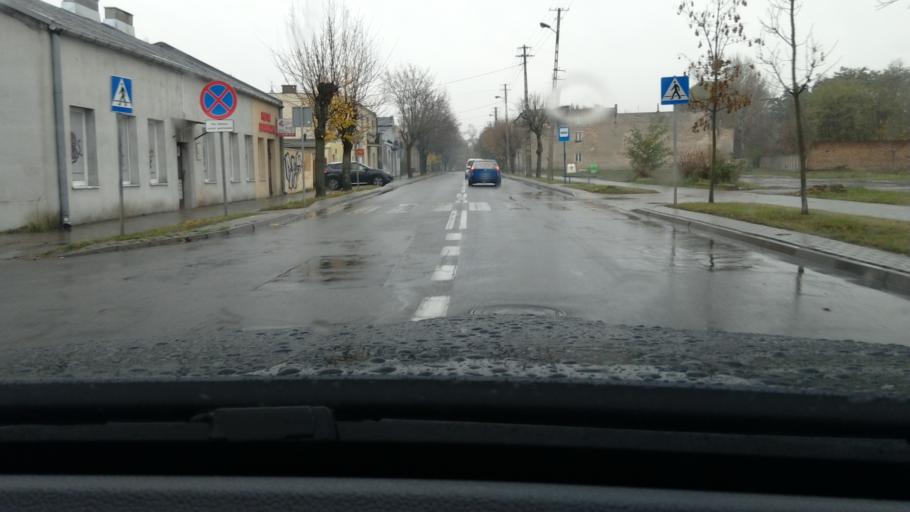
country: PL
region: Lodz Voivodeship
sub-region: Skierniewice
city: Skierniewice
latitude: 51.9519
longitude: 20.1427
